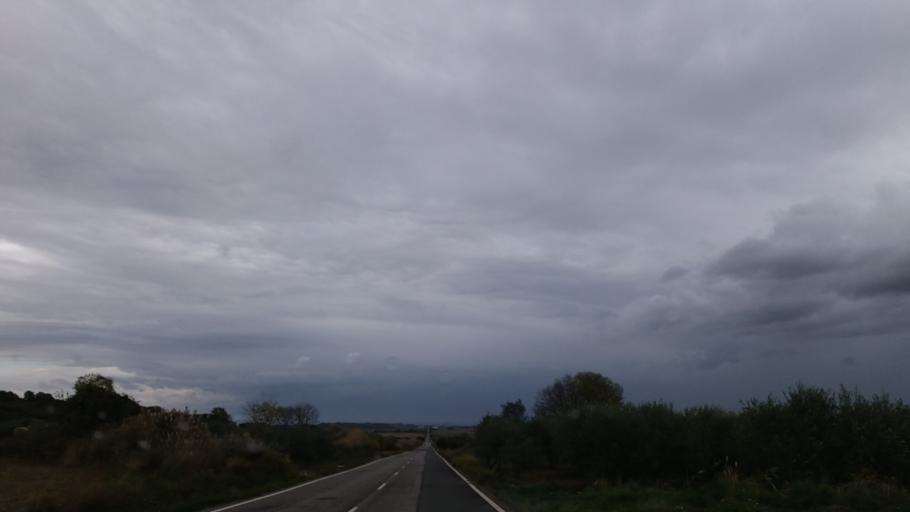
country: ES
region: Catalonia
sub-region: Provincia de Lleida
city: Castello de Farfanya
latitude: 41.8141
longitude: 0.7386
